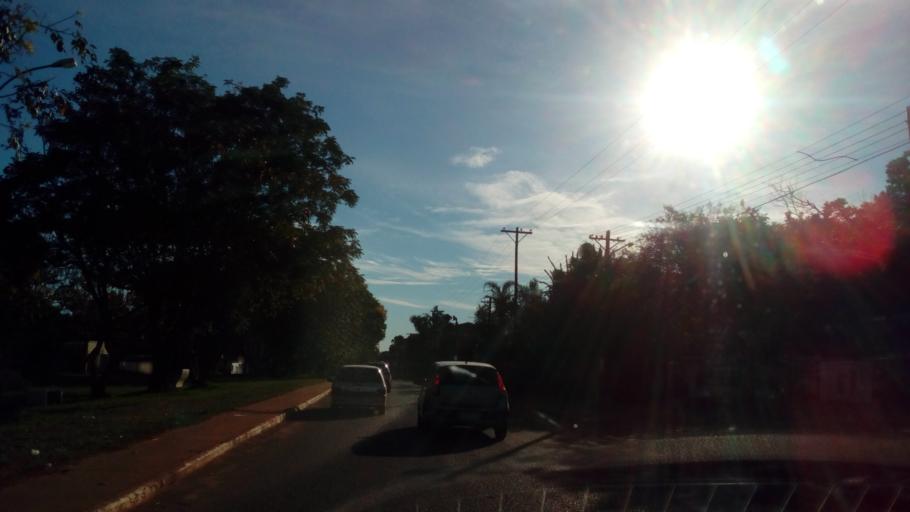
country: AR
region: Misiones
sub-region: Departamento de Capital
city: Posadas
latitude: -27.4309
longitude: -55.8832
